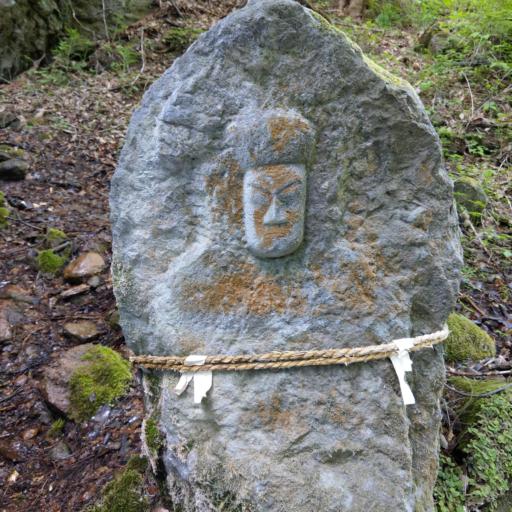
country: JP
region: Nagano
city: Komoro
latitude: 36.3690
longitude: 138.4497
